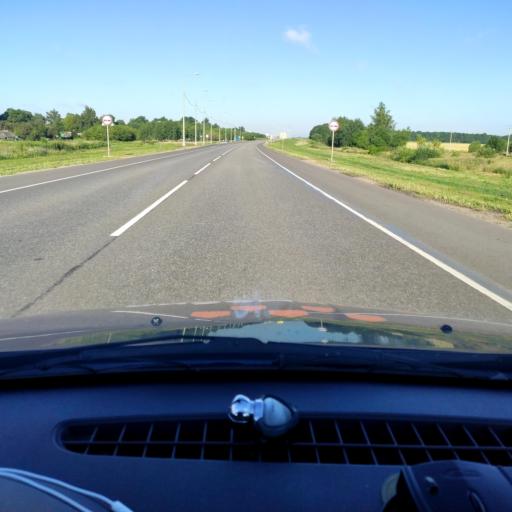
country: RU
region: Orjol
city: Pokrovskoye
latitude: 52.6227
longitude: 36.7903
